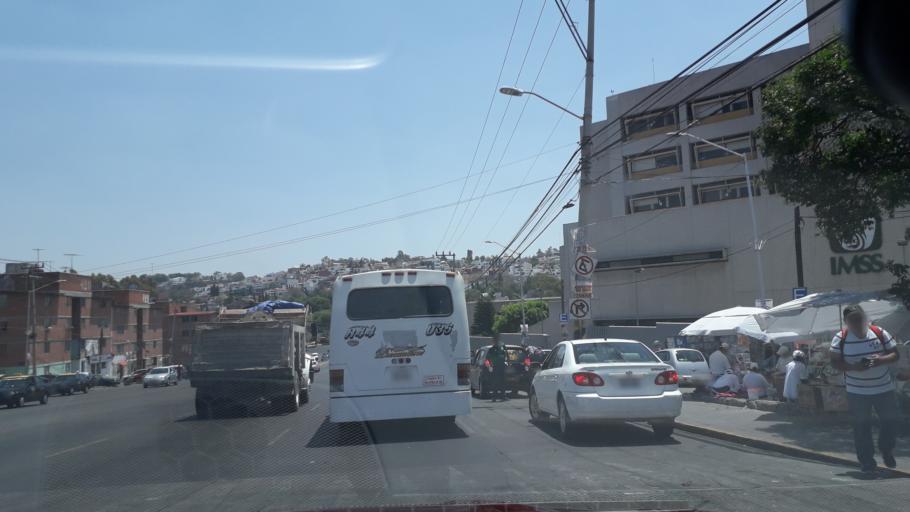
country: MX
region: Puebla
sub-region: Puebla
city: Galaxia la Calera
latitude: 19.0094
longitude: -98.1836
